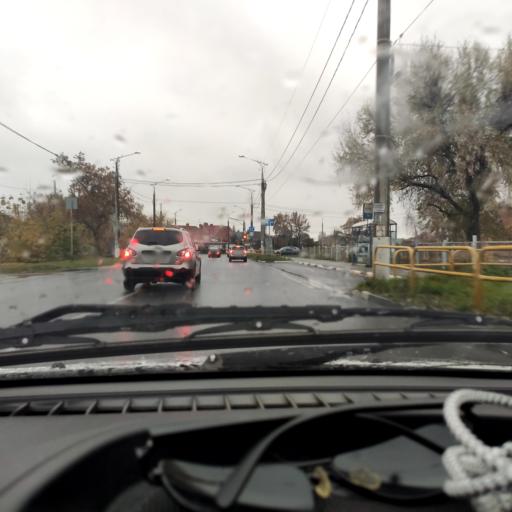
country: RU
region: Samara
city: Tol'yatti
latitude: 53.5112
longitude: 49.3952
